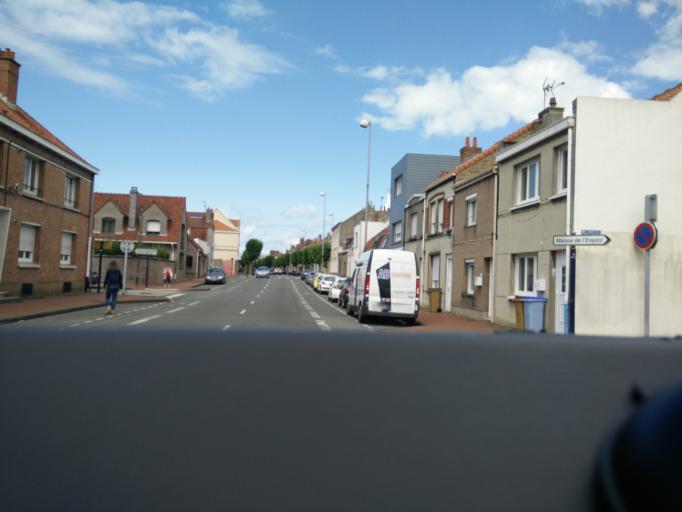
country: FR
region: Nord-Pas-de-Calais
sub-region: Departement du Nord
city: Coudekerque-Branche
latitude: 51.0425
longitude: 2.4047
